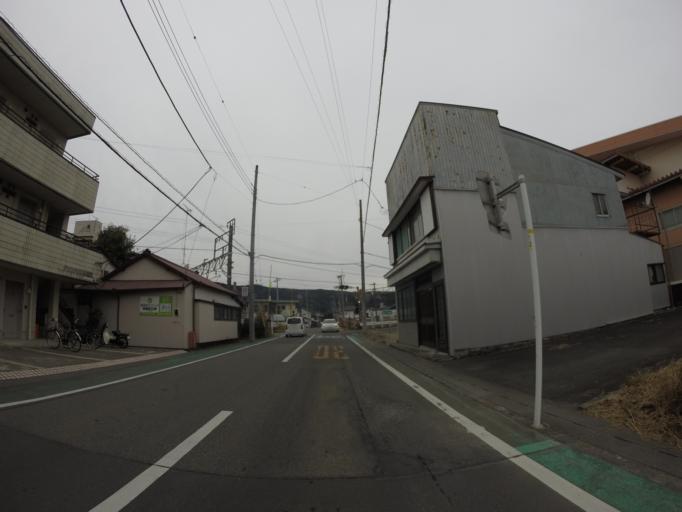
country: JP
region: Shizuoka
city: Fujinomiya
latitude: 35.2264
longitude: 138.6022
